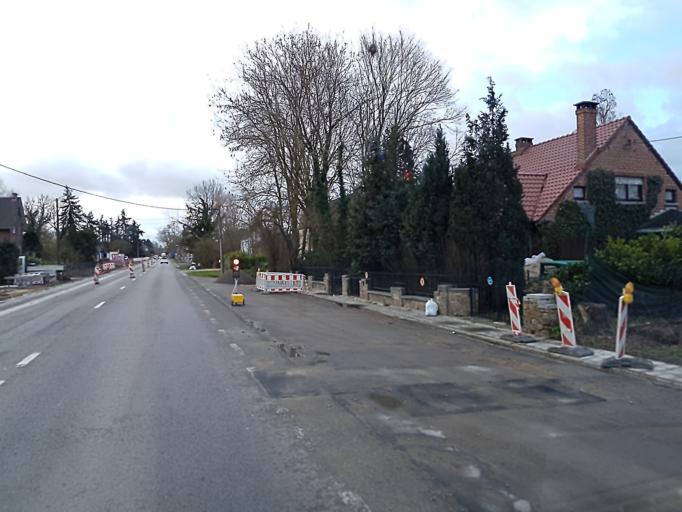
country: BE
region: Wallonia
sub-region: Province du Brabant Wallon
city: Jodoigne
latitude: 50.7418
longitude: 4.8797
